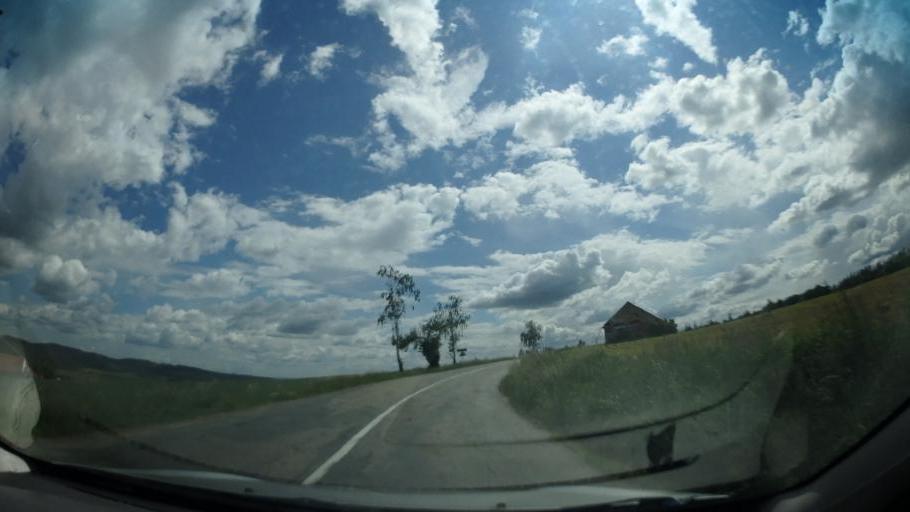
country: CZ
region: South Moravian
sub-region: Okres Blansko
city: Letovice
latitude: 49.5843
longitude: 16.5915
